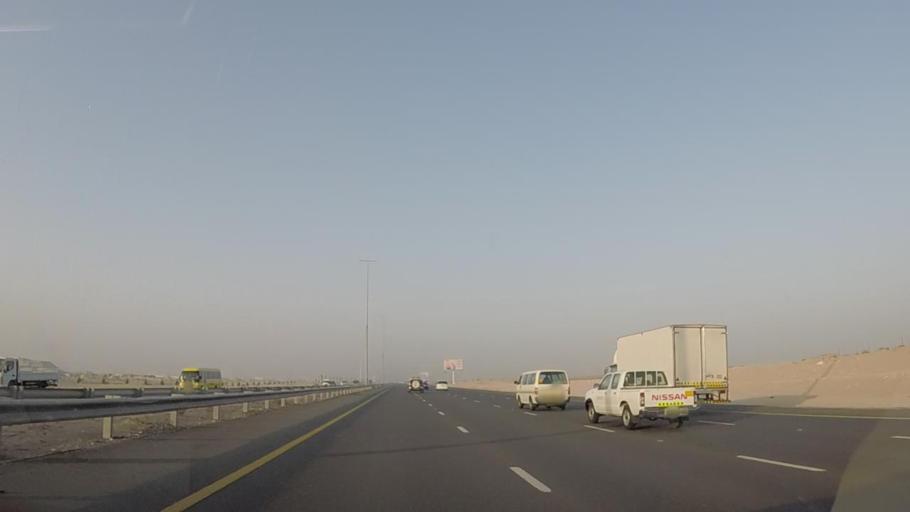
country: AE
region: Dubai
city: Dubai
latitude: 24.9355
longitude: 55.0289
